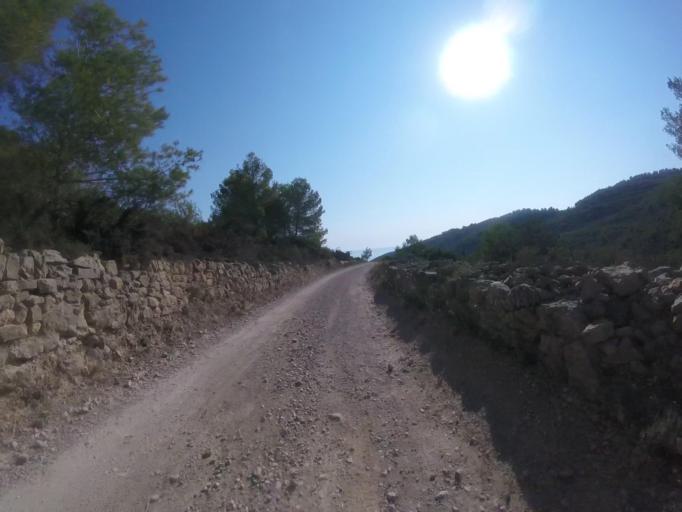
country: ES
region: Valencia
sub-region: Provincia de Castello
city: Santa Magdalena de Pulpis
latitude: 40.3284
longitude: 0.3543
